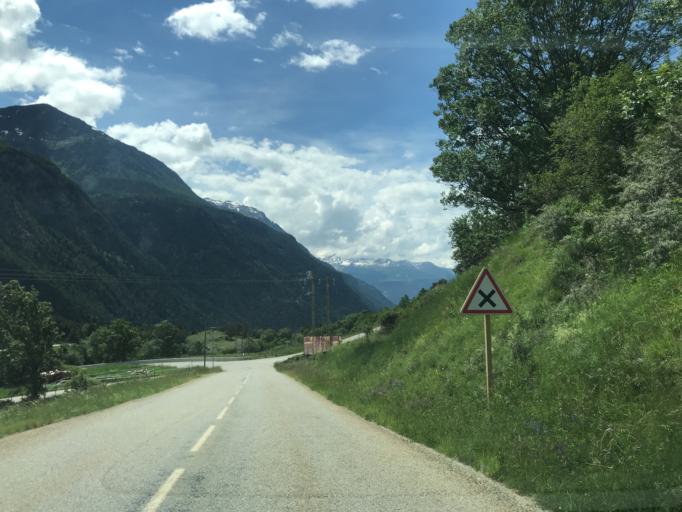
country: FR
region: Rhone-Alpes
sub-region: Departement de la Savoie
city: Modane
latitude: 45.2043
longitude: 6.6160
